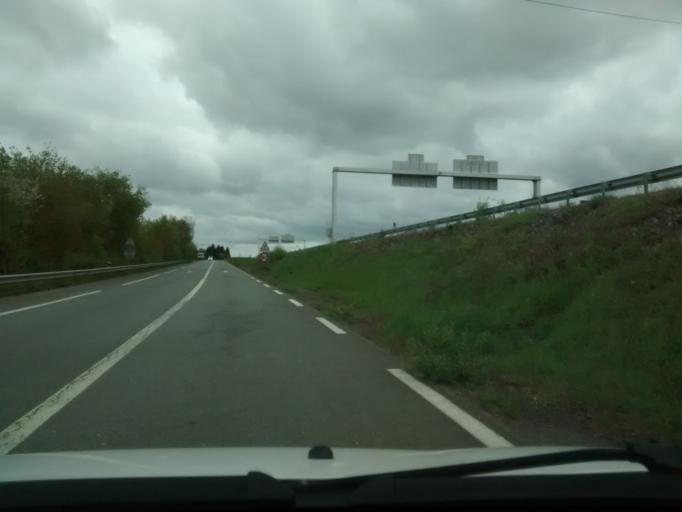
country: FR
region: Brittany
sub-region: Departement d'Ille-et-Vilaine
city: Cesson-Sevigne
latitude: 48.1139
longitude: -1.5776
